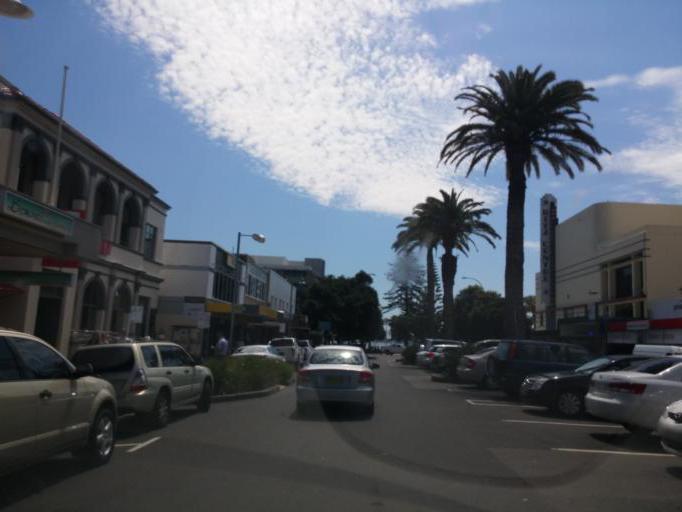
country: AU
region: New South Wales
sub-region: Port Macquarie-Hastings
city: Port Macquarie
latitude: -31.4300
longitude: 152.9082
